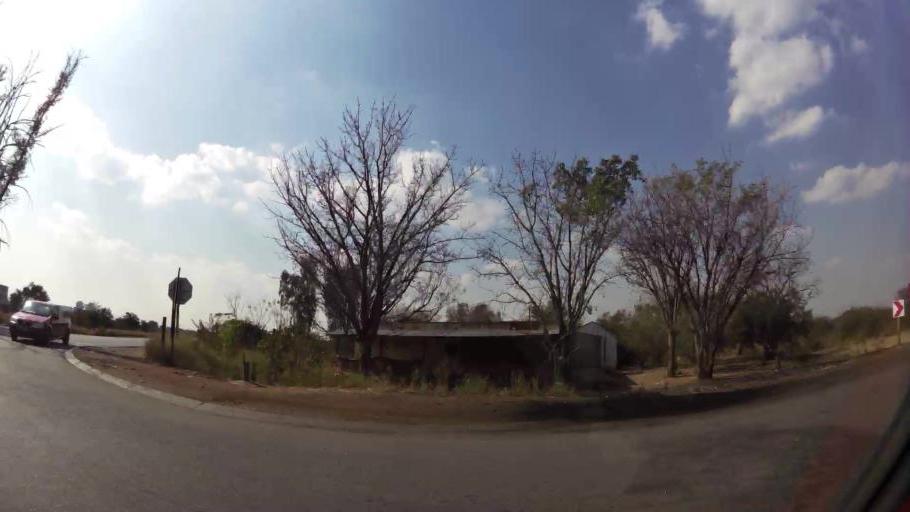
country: ZA
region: North-West
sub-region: Bojanala Platinum District Municipality
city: Rustenburg
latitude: -25.5054
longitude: 27.0986
